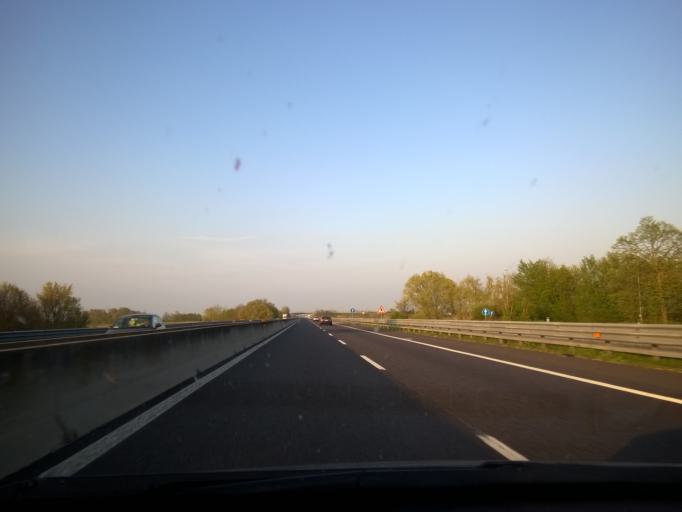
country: IT
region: Veneto
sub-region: Provincia di Rovigo
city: Fiesso Umbertiano
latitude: 44.9341
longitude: 11.6109
